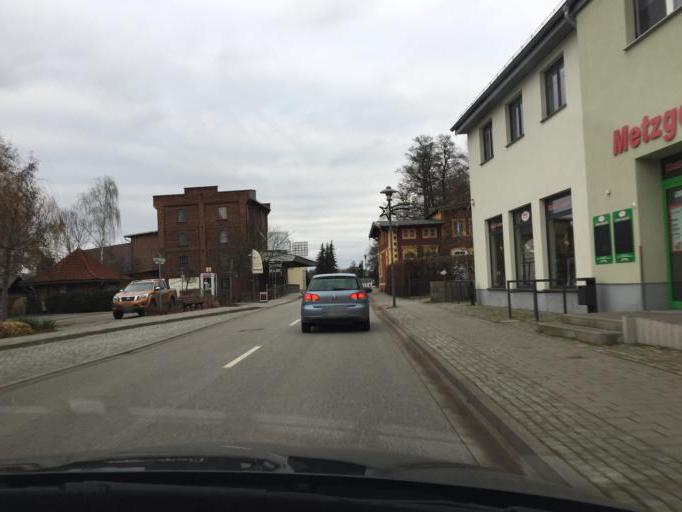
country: DE
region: Brandenburg
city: Burg
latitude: 51.8366
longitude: 14.1487
